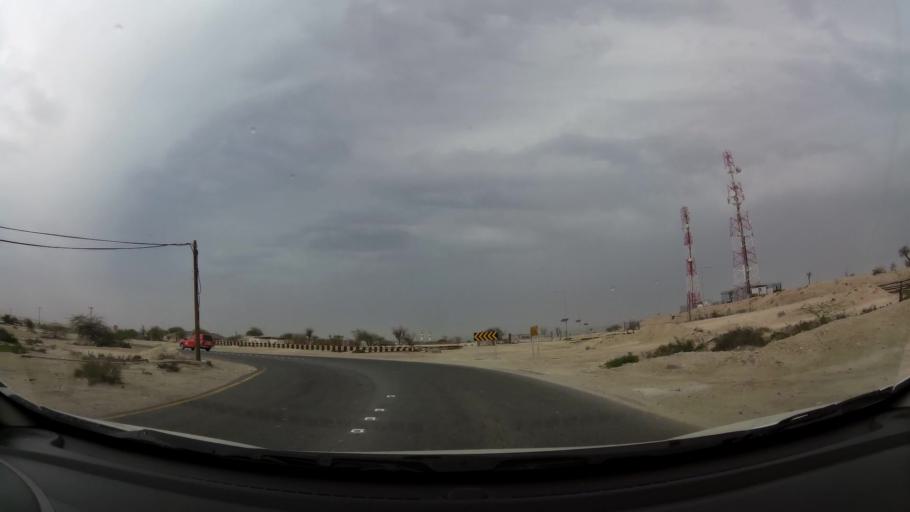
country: BH
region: Central Governorate
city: Dar Kulayb
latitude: 26.0789
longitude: 50.5488
